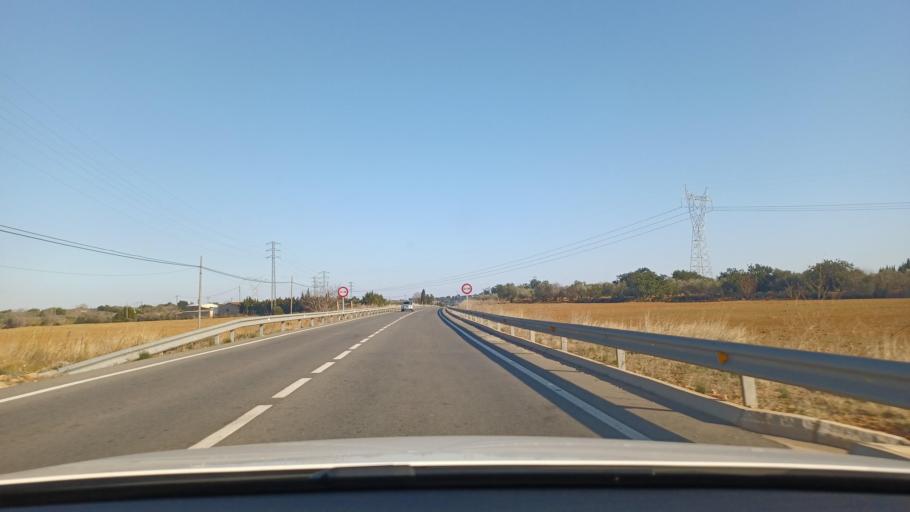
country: ES
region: Catalonia
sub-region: Provincia de Tarragona
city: Masdenverge
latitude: 40.7173
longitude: 0.5160
